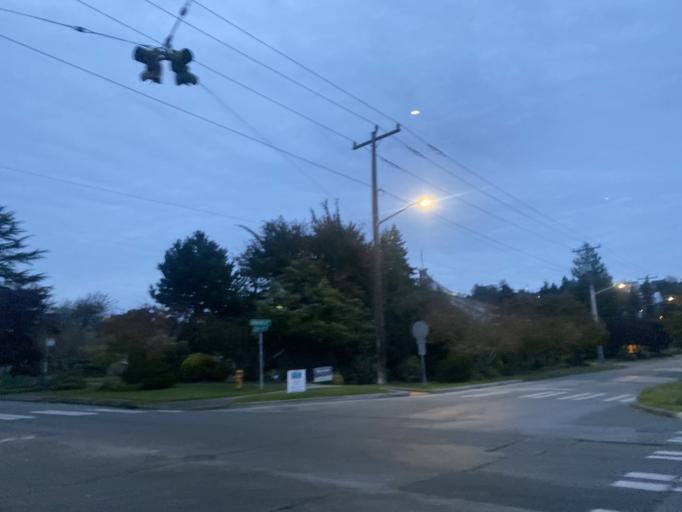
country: US
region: Washington
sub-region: King County
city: Seattle
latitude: 47.6468
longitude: -122.4010
